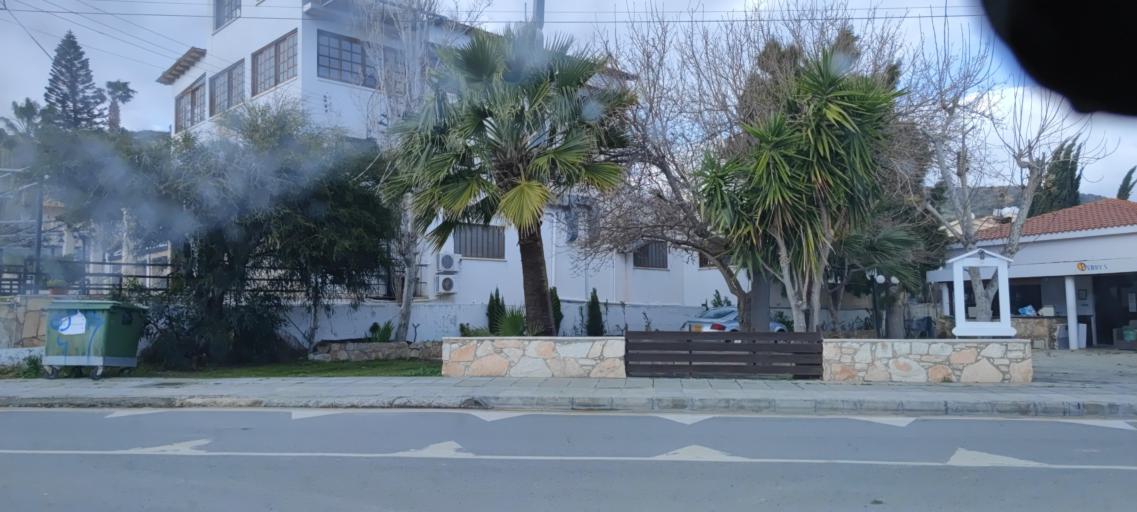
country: CY
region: Limassol
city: Pissouri
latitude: 34.6510
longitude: 32.7236
